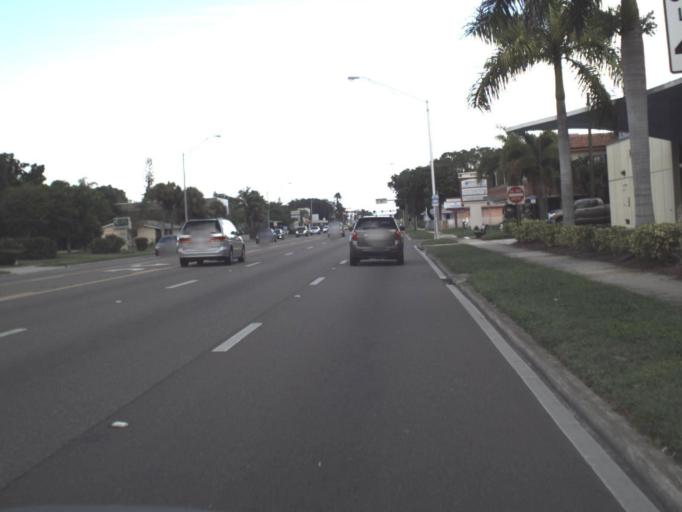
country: US
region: Florida
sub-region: Sarasota County
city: South Sarasota
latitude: 27.3049
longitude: -82.5301
